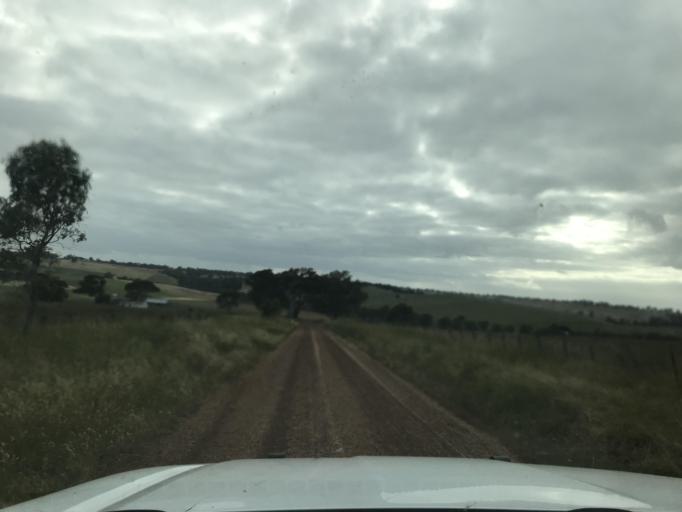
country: AU
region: South Australia
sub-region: Wattle Range
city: Penola
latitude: -37.2799
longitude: 141.3976
